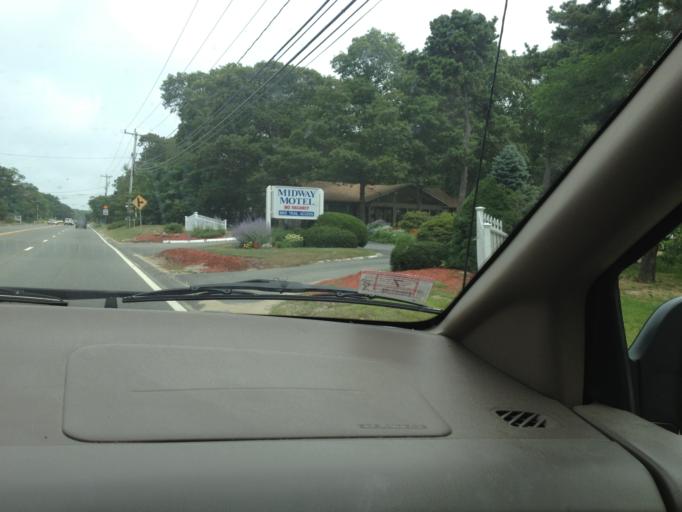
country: US
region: Massachusetts
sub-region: Barnstable County
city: North Eastham
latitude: 41.8696
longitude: -69.9853
